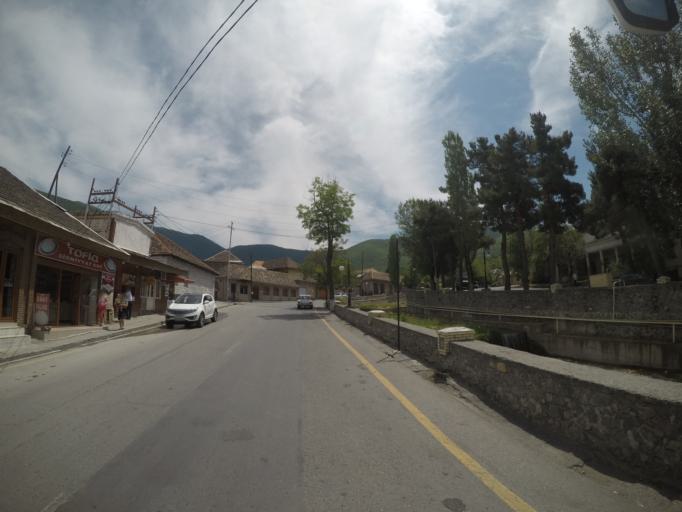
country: AZ
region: Shaki City
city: Sheki
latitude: 41.2014
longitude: 47.1839
